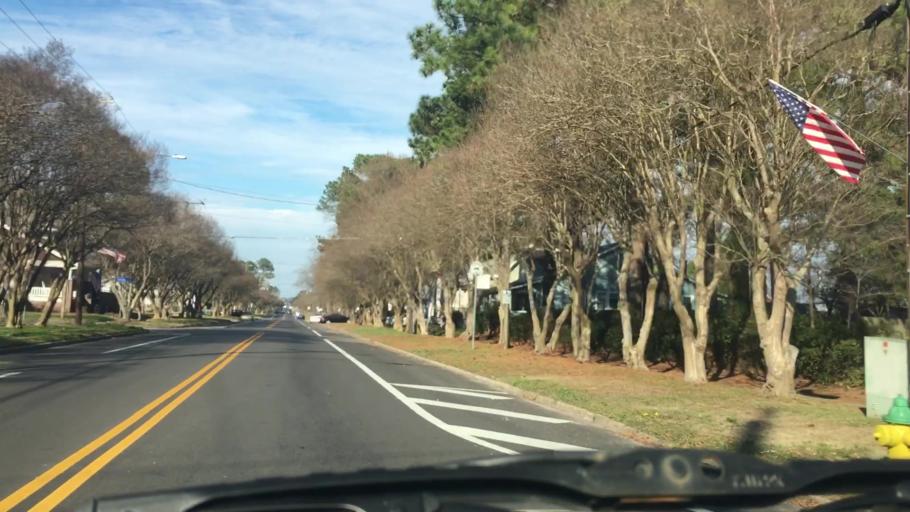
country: US
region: Virginia
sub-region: City of Norfolk
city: Norfolk
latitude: 36.8622
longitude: -76.2502
